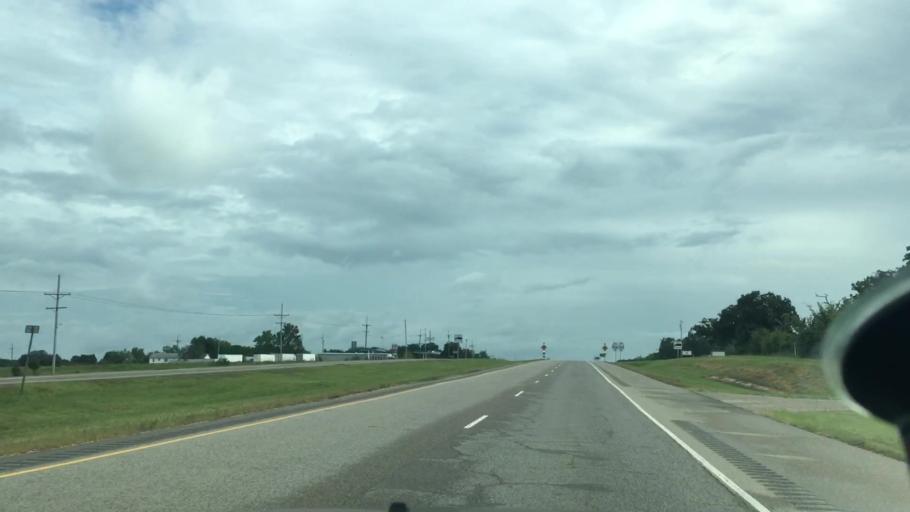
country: US
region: Oklahoma
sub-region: Seminole County
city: Seminole
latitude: 35.3522
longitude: -96.6718
